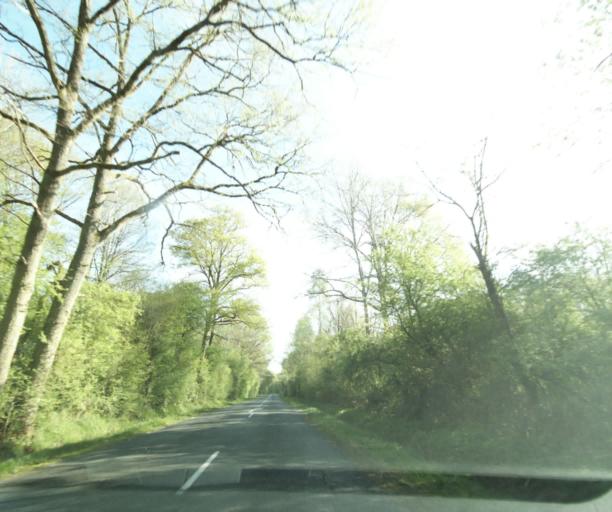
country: FR
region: Ile-de-France
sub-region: Departement de Seine-et-Marne
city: La Chapelle-Gauthier
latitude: 48.4892
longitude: 2.8865
